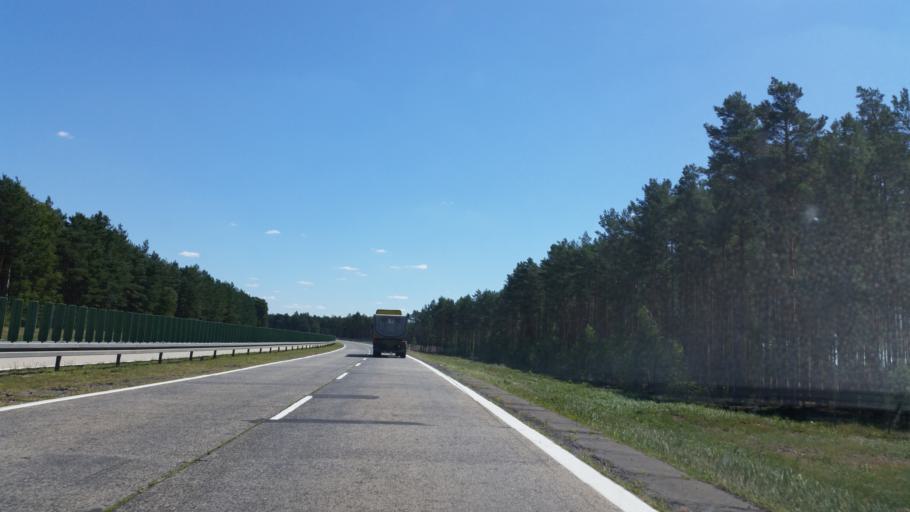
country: PL
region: Lubusz
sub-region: Powiat zaganski
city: Malomice
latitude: 51.4345
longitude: 15.3686
